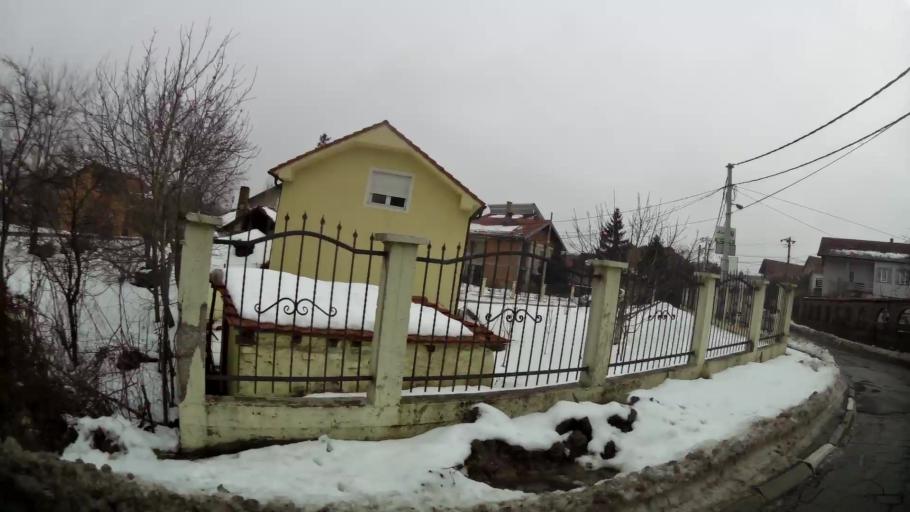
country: RS
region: Central Serbia
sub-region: Belgrade
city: Zvezdara
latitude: 44.7615
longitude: 20.5268
